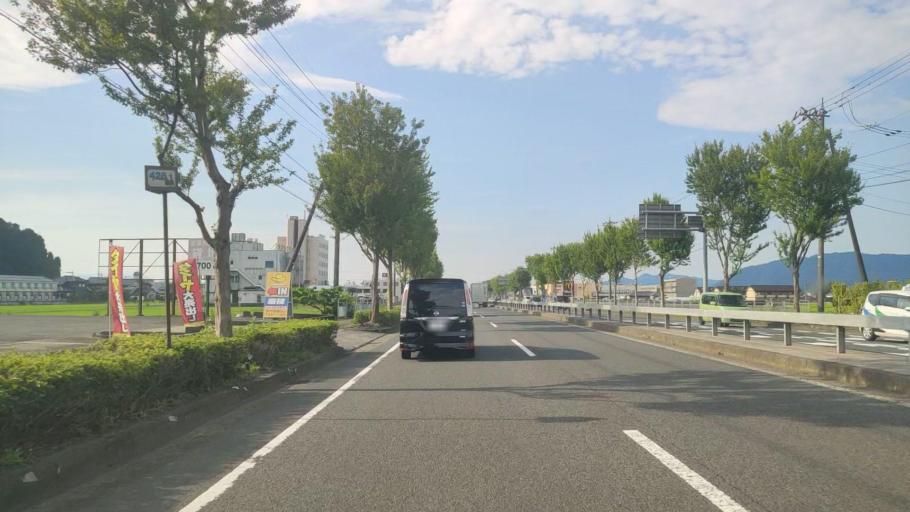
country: JP
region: Fukui
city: Takefu
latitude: 35.9028
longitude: 136.1922
